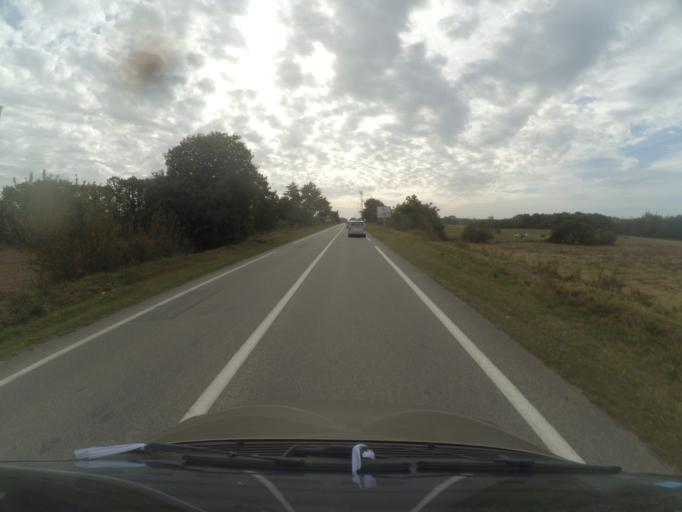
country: FR
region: Brittany
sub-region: Departement du Morbihan
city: Sainte-Helene
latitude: 47.7090
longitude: -3.2209
